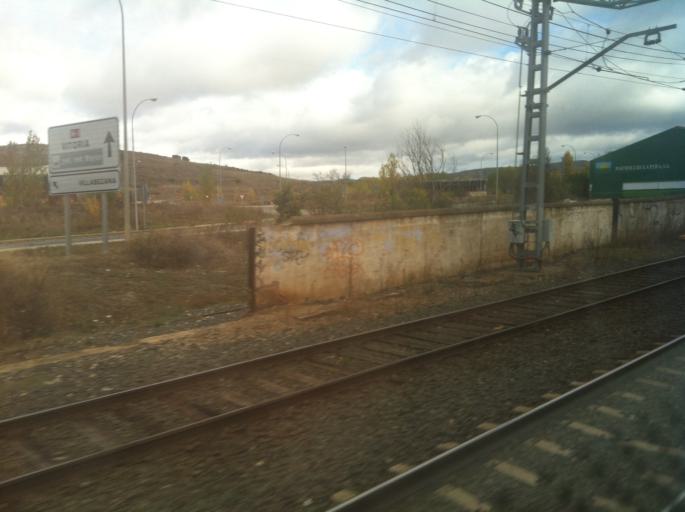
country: ES
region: Castille and Leon
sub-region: Provincia de Burgos
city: Miranda de Ebro
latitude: 42.6936
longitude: -2.9338
